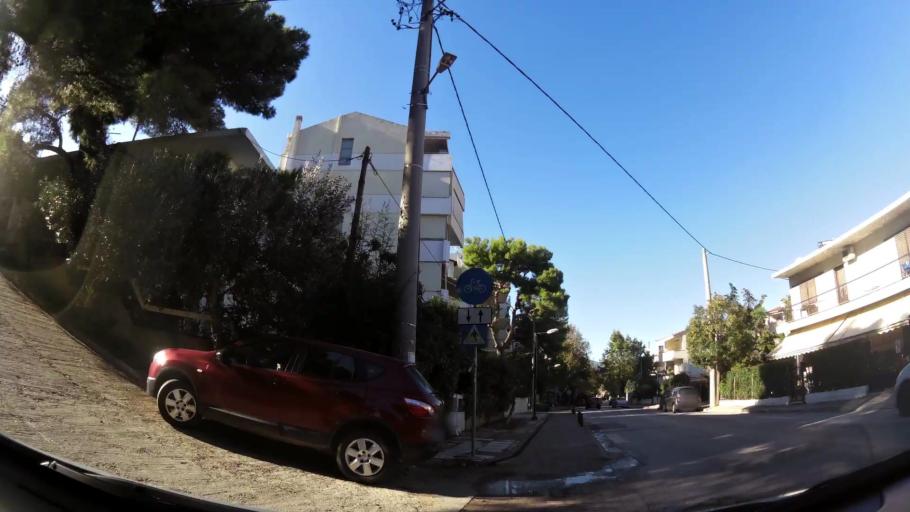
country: GR
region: Attica
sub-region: Nomarchia Athinas
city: Nea Erythraia
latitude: 38.0943
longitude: 23.8146
